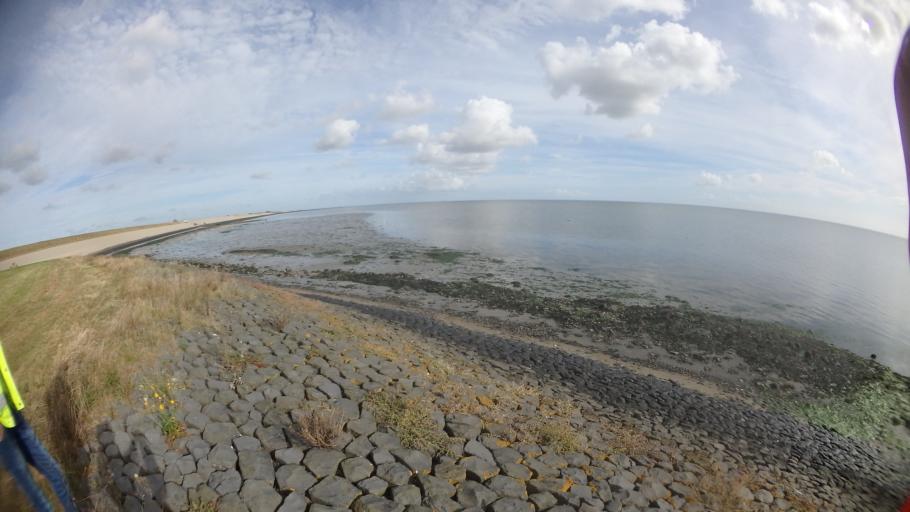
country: NL
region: North Holland
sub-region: Gemeente Texel
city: Den Burg
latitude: 53.0975
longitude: 4.8995
